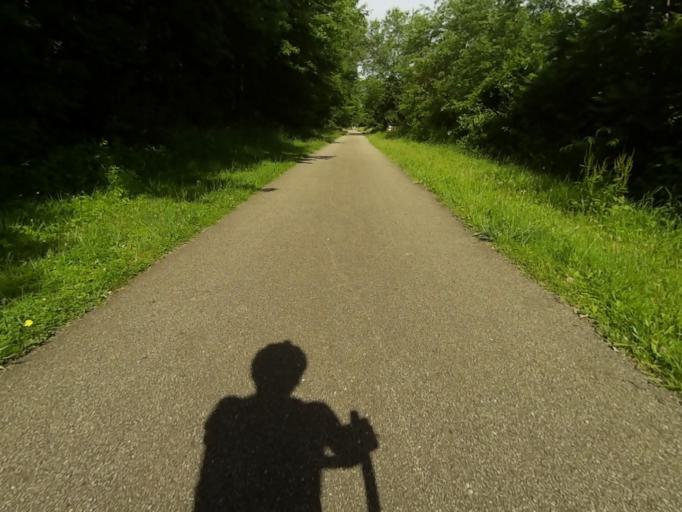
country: US
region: Ohio
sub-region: Summit County
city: Stow
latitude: 41.1925
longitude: -81.4108
